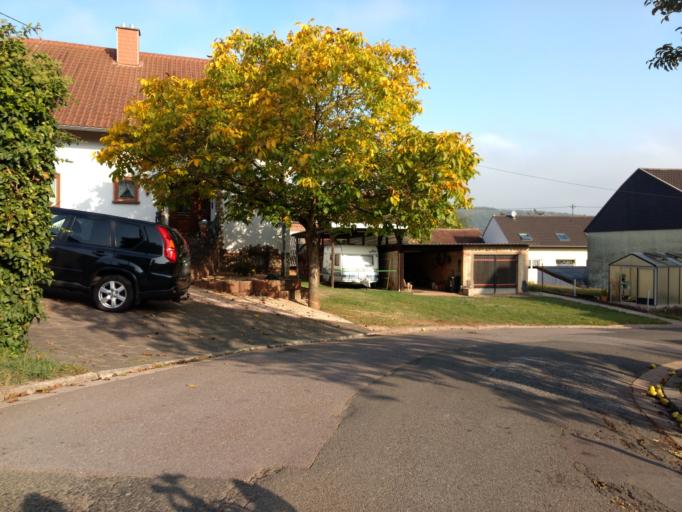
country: DE
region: Saarland
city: Saarwellingen
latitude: 49.3844
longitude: 6.8250
